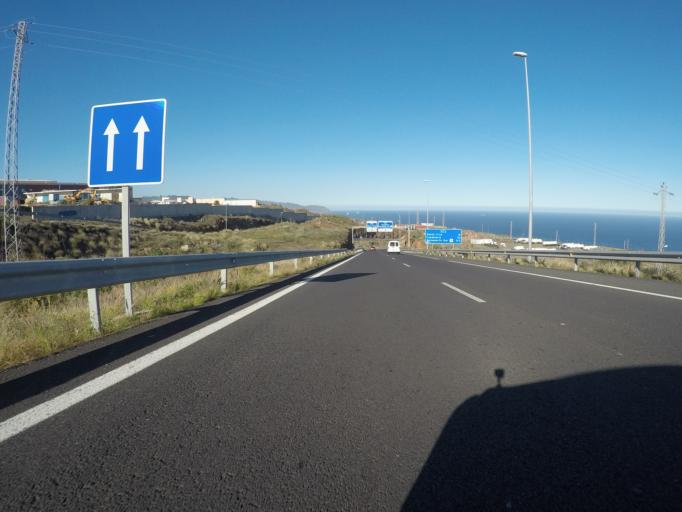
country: ES
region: Canary Islands
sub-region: Provincia de Santa Cruz de Tenerife
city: La Laguna
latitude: 28.4197
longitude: -16.3190
